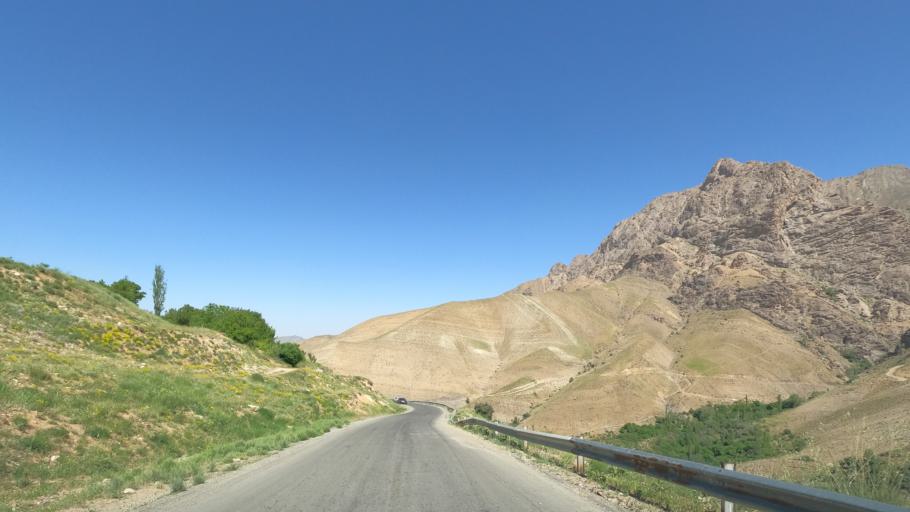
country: IR
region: Alborz
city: Karaj
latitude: 35.9229
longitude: 51.1624
